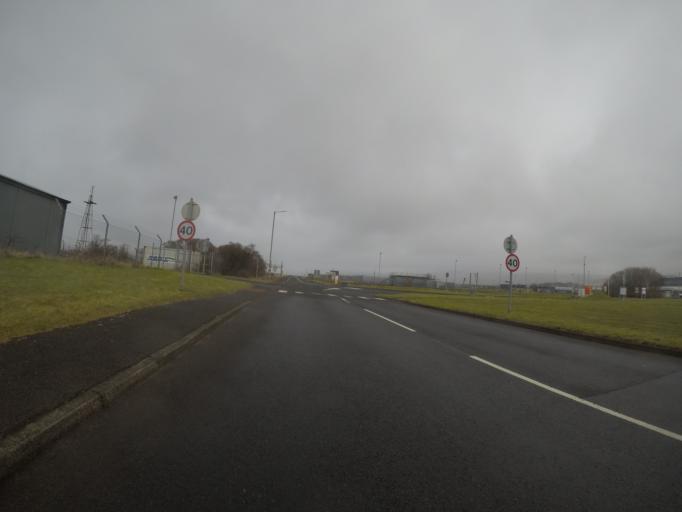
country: GB
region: Scotland
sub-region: North Ayrshire
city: Millport
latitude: 55.7230
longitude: -4.8989
